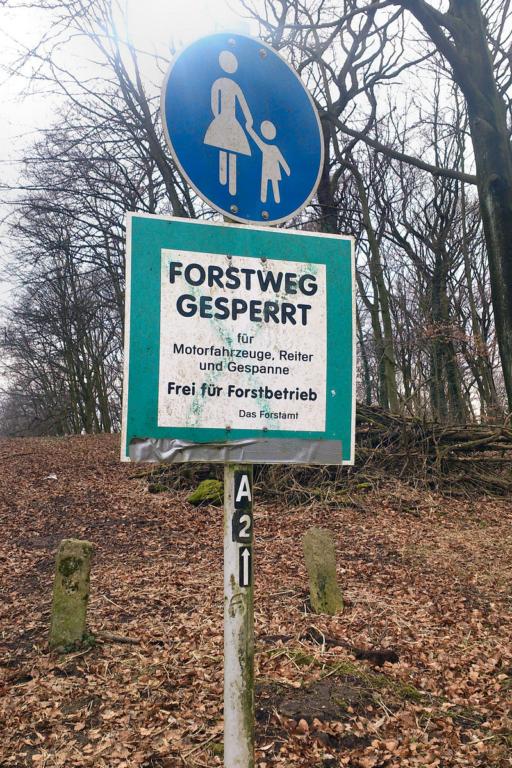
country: DE
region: North Rhine-Westphalia
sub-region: Regierungsbezirk Dusseldorf
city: Duisburg
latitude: 51.4313
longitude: 6.8184
